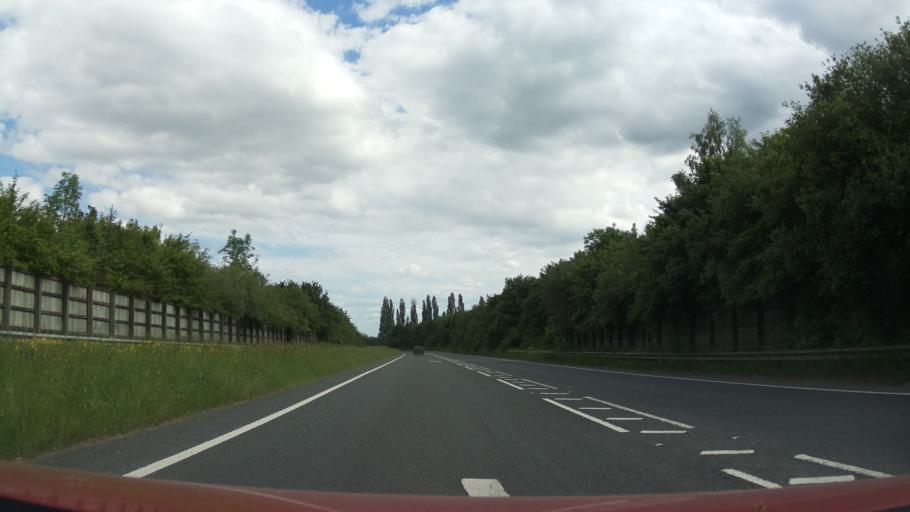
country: GB
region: England
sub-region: Worcestershire
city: Bransford
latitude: 52.1853
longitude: -2.2635
